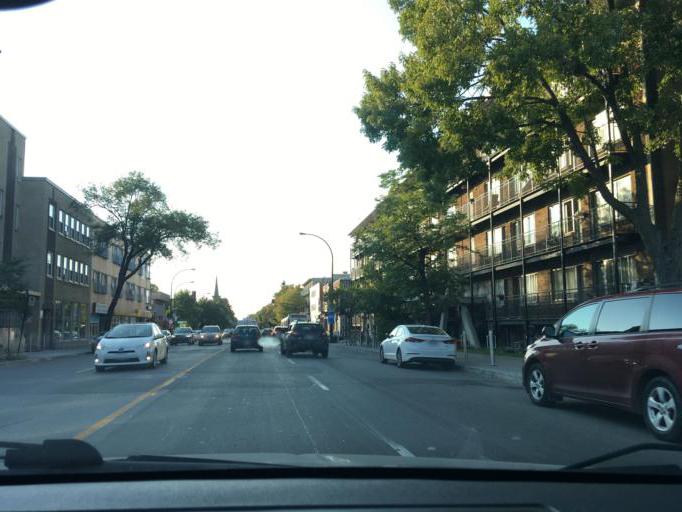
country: CA
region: Quebec
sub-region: Montreal
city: Montreal
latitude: 45.5459
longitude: -73.6024
